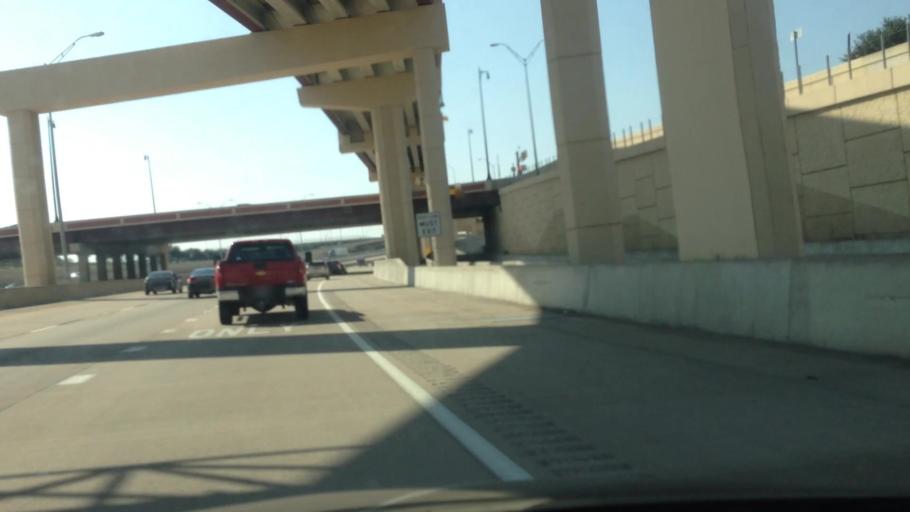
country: US
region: Texas
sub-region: Tarrant County
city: Grapevine
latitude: 32.9248
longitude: -97.0871
